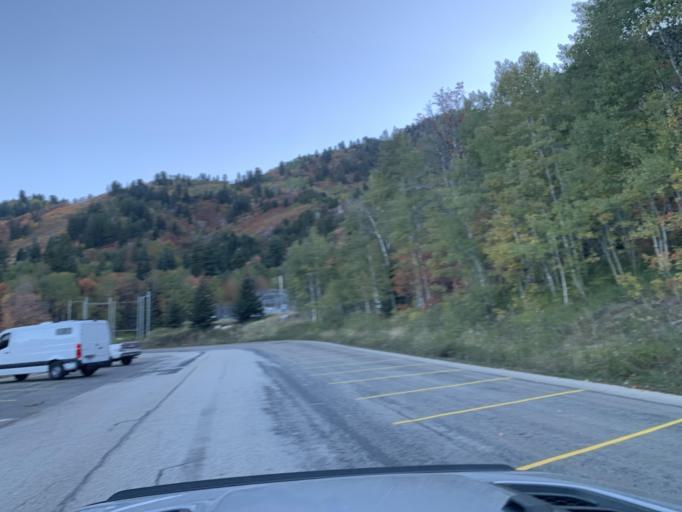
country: US
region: Utah
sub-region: Weber County
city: Uintah
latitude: 41.2178
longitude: -111.8634
